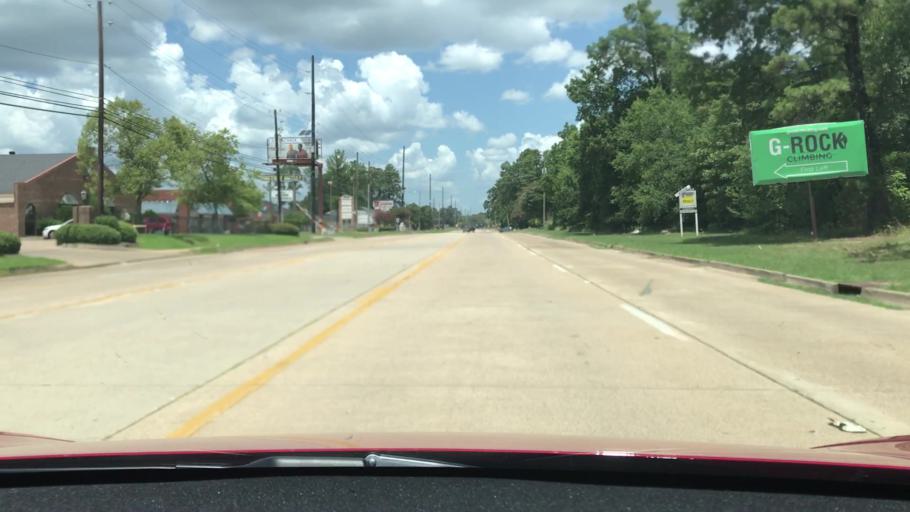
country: US
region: Louisiana
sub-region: Bossier Parish
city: Bossier City
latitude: 32.4234
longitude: -93.7381
